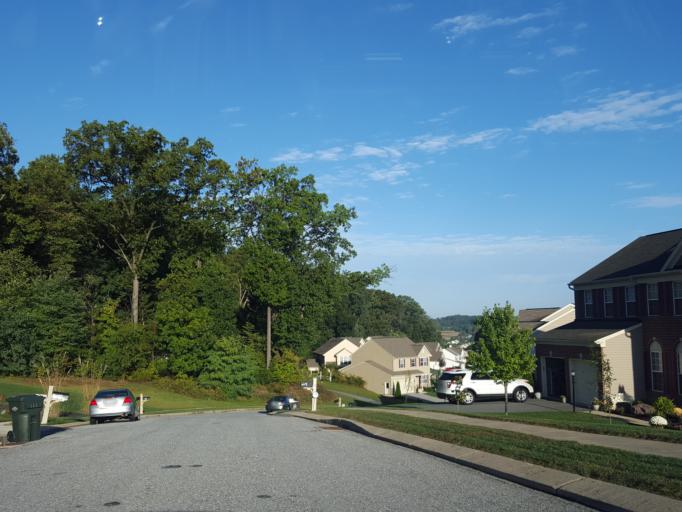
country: US
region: Pennsylvania
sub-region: York County
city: Windsor
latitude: 39.9468
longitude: -76.6086
